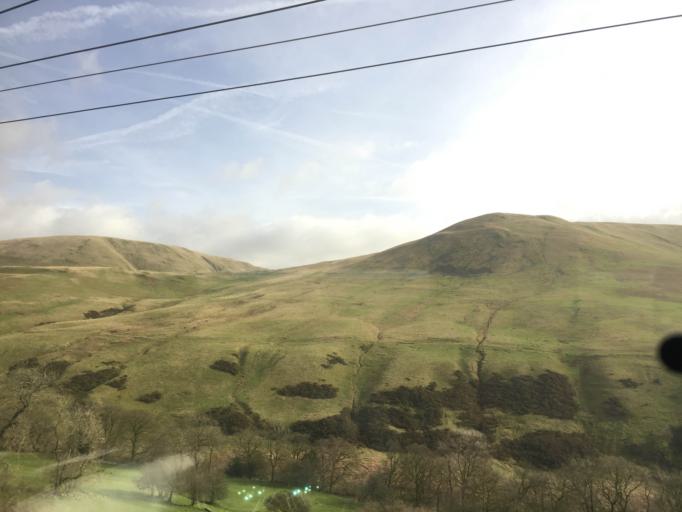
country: GB
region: England
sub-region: Cumbria
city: Sedbergh
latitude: 54.3802
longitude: -2.5806
